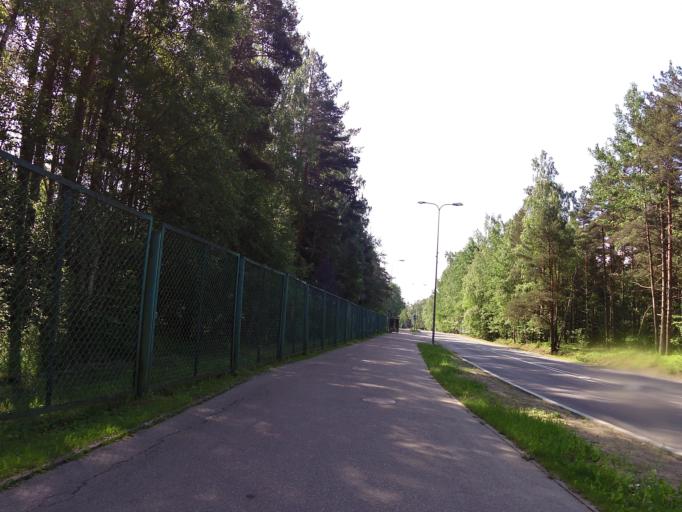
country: EE
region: Harju
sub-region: Saue vald
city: Laagri
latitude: 59.4381
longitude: 24.6269
